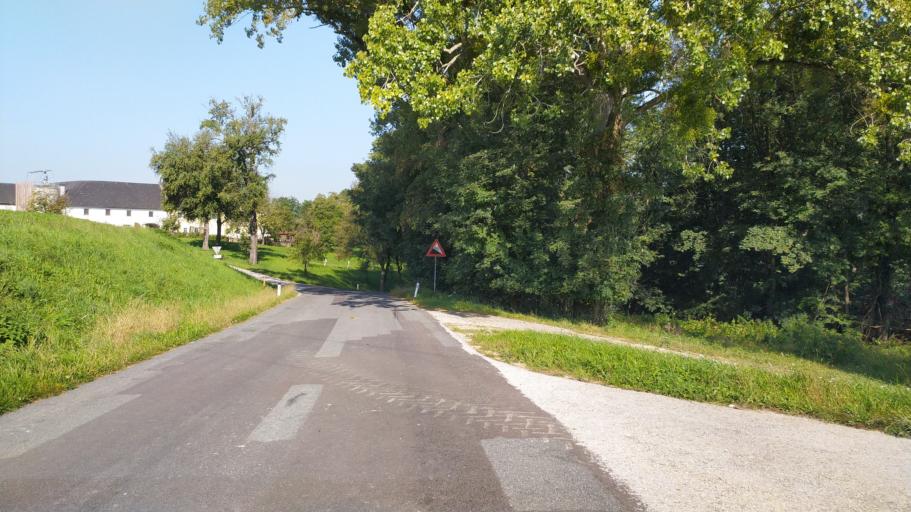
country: AT
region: Lower Austria
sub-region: Politischer Bezirk Amstetten
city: Zeillern
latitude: 48.1521
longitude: 14.7470
